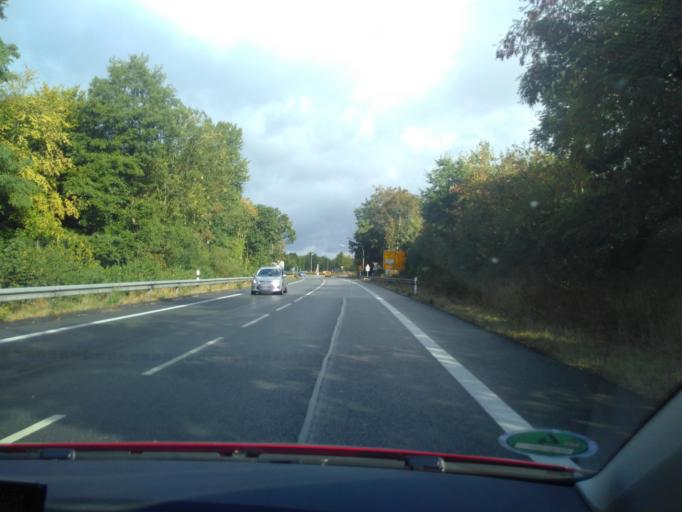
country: DE
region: North Rhine-Westphalia
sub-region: Regierungsbezirk Munster
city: Warendorf
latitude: 51.9563
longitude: 8.0128
